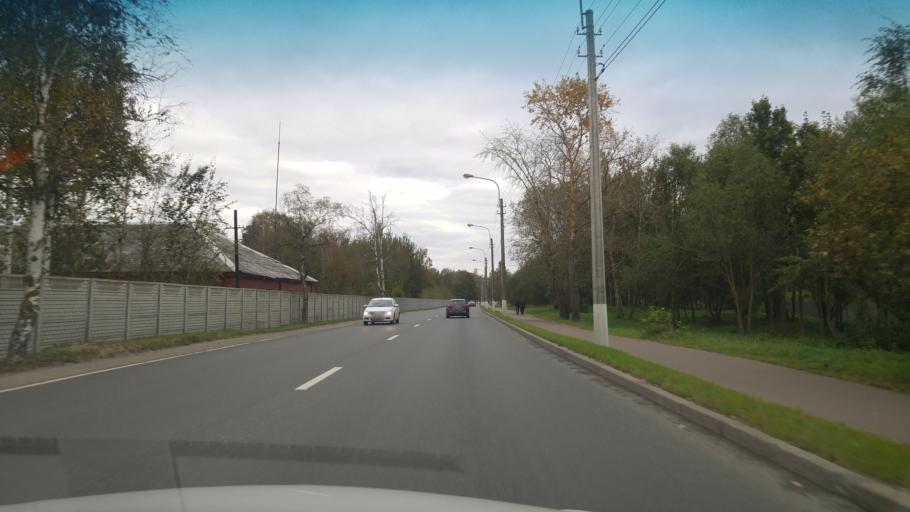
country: RU
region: St.-Petersburg
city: Kronshtadt
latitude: 60.0064
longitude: 29.7432
